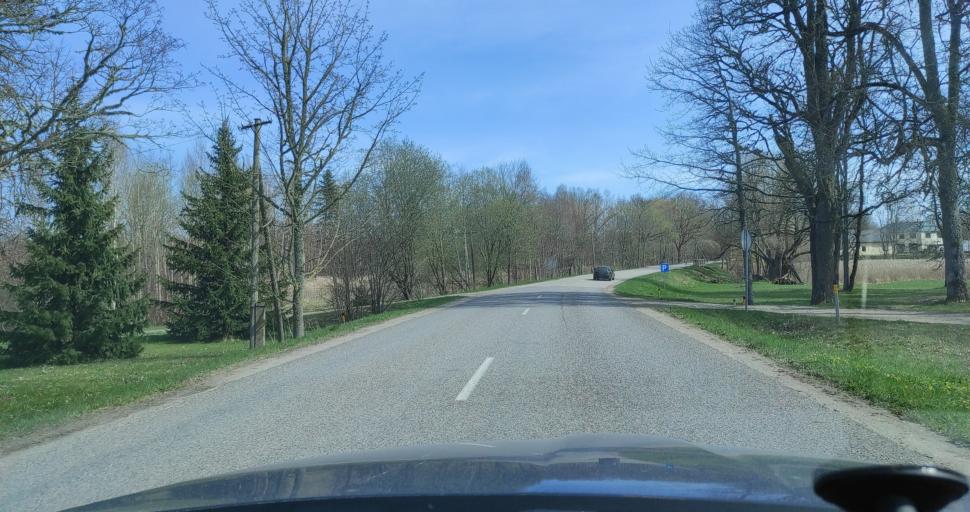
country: LV
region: Talsu Rajons
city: Talsi
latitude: 57.2244
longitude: 22.5148
